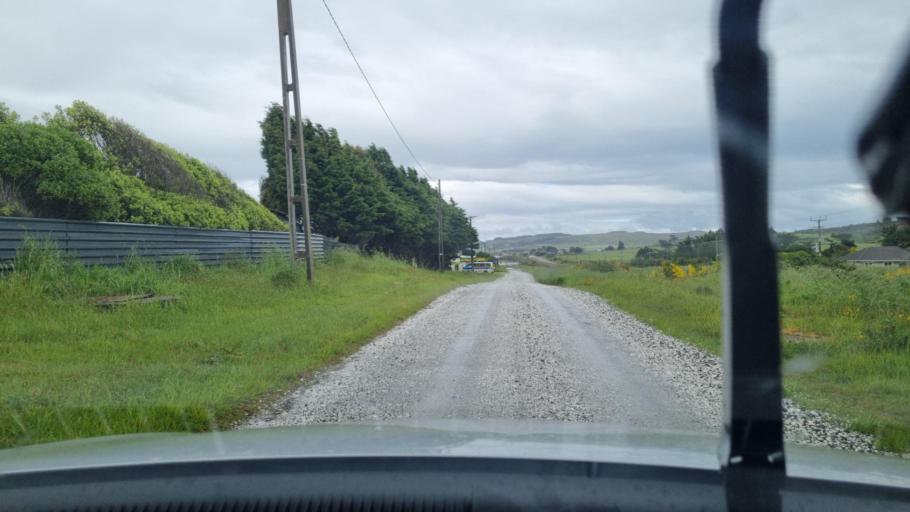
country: NZ
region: Southland
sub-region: Invercargill City
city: Bluff
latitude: -46.5447
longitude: 168.3014
